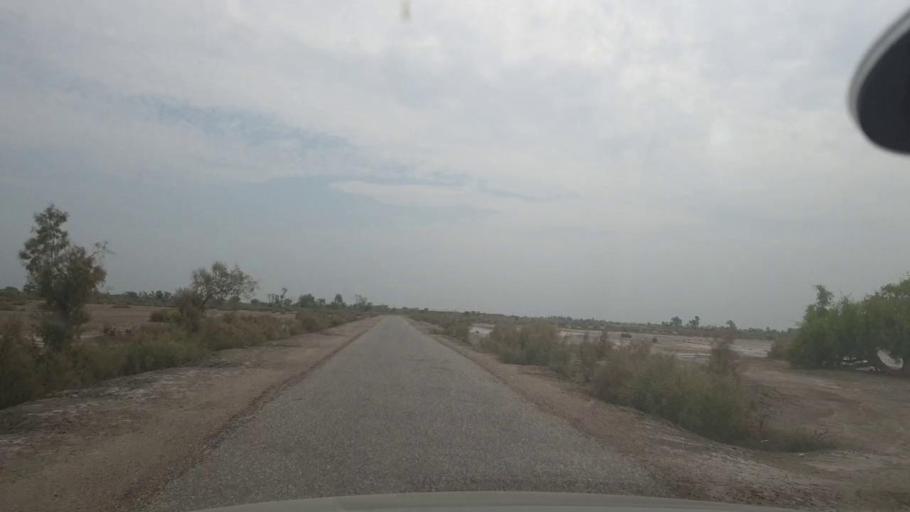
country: PK
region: Balochistan
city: Mehrabpur
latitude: 28.0586
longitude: 68.1376
